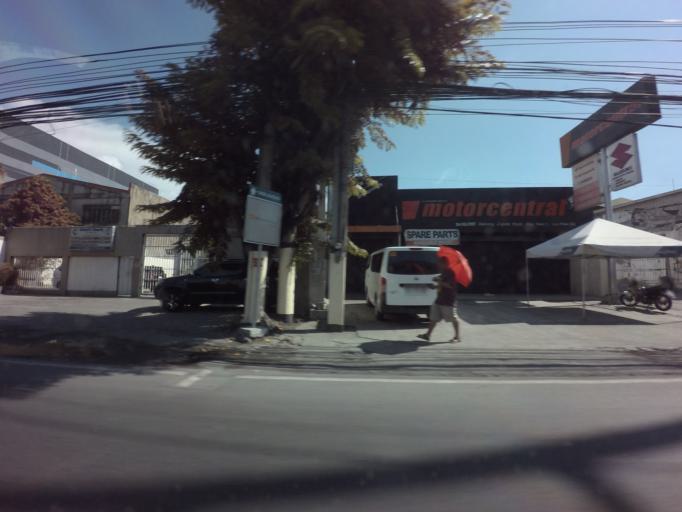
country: PH
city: Sambayanihan People's Village
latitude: 14.4438
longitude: 120.9950
